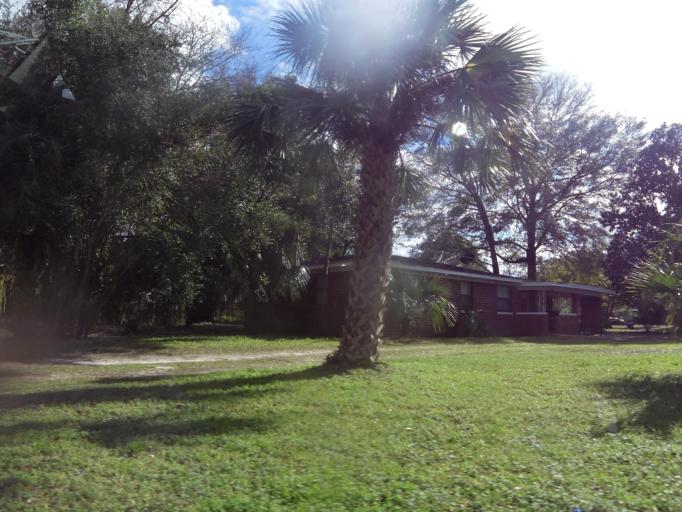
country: US
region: Florida
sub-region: Duval County
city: Jacksonville
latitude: 30.3421
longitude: -81.5961
